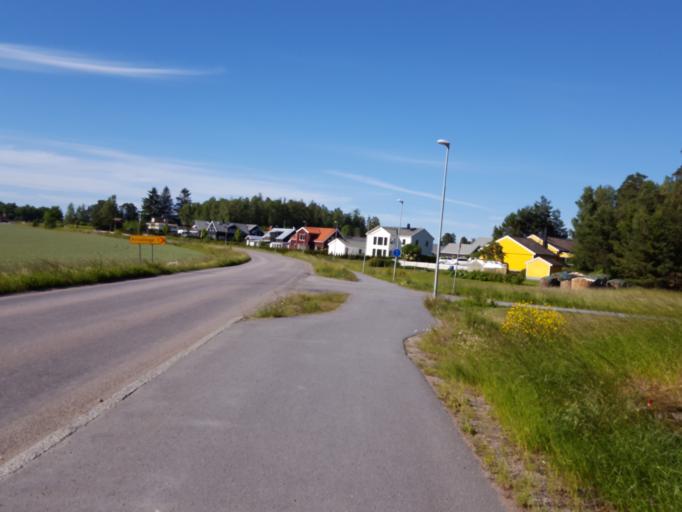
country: SE
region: Uppsala
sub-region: Uppsala Kommun
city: Saevja
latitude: 59.8339
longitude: 17.7443
